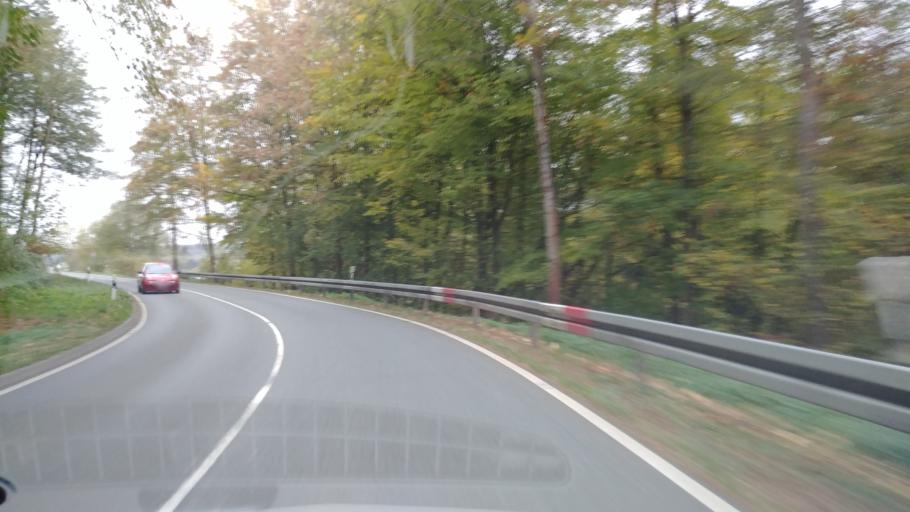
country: DE
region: Hesse
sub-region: Regierungsbezirk Darmstadt
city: Idstein
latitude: 50.2504
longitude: 8.2130
